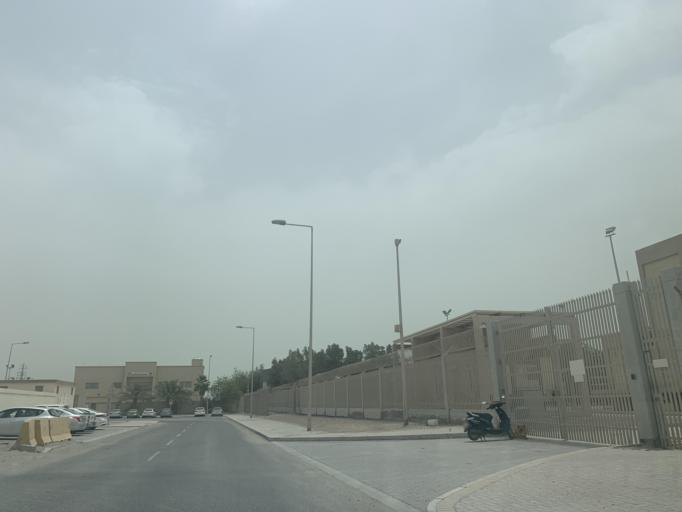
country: BH
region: Northern
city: Sitrah
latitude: 26.1852
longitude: 50.6217
